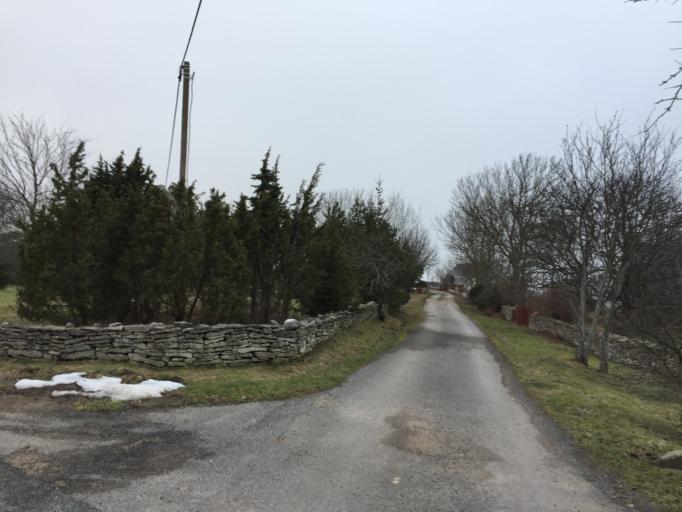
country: EE
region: Saare
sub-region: Kuressaare linn
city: Kuressaare
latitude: 58.5449
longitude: 22.2169
